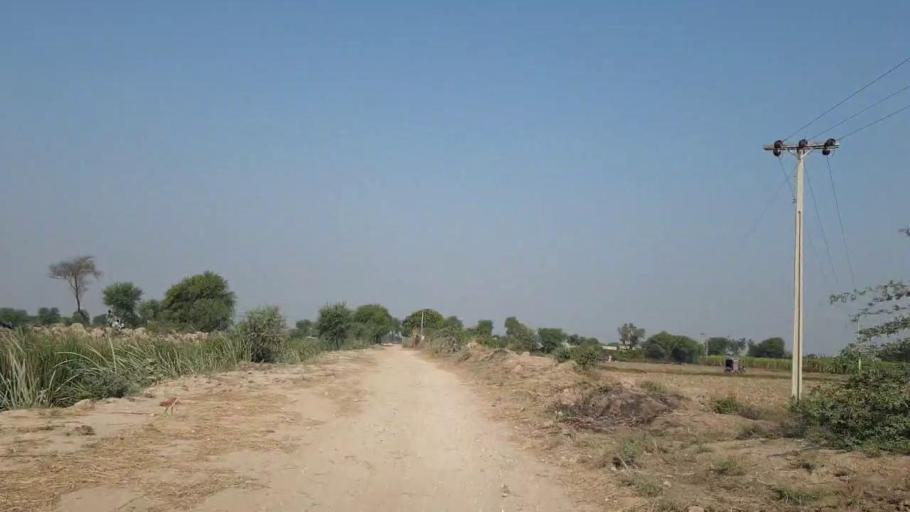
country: PK
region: Sindh
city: Matli
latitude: 24.9876
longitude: 68.6260
